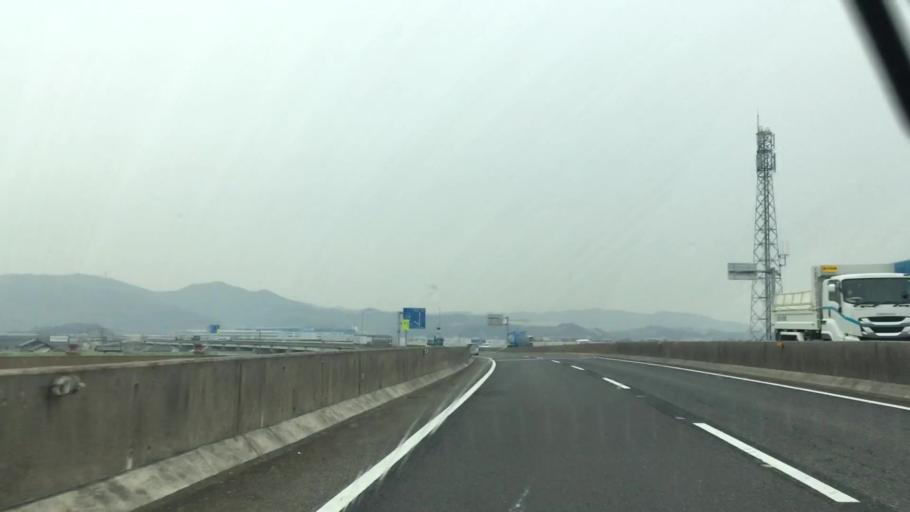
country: JP
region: Aichi
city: Nishio
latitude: 34.8728
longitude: 137.0829
